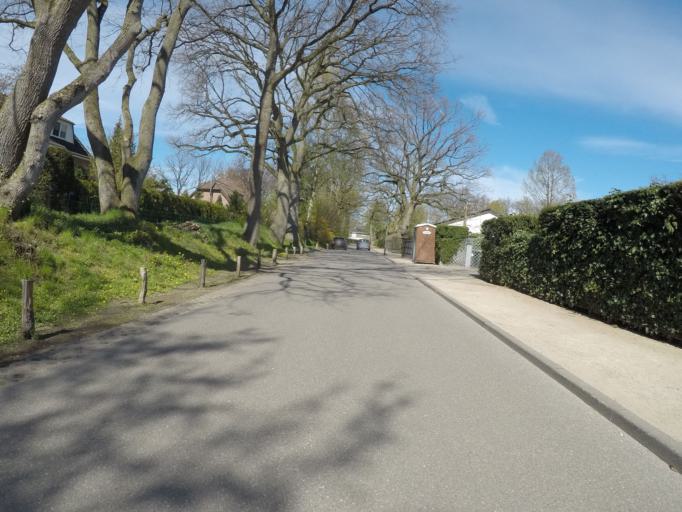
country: DE
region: Hamburg
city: Lemsahl-Mellingstedt
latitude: 53.6743
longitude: 10.1030
